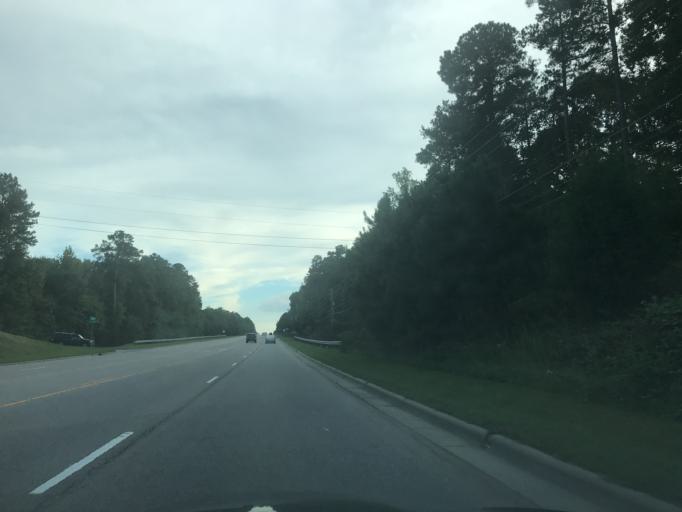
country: US
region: North Carolina
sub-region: Wake County
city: Green Level
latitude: 35.7694
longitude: -78.8741
